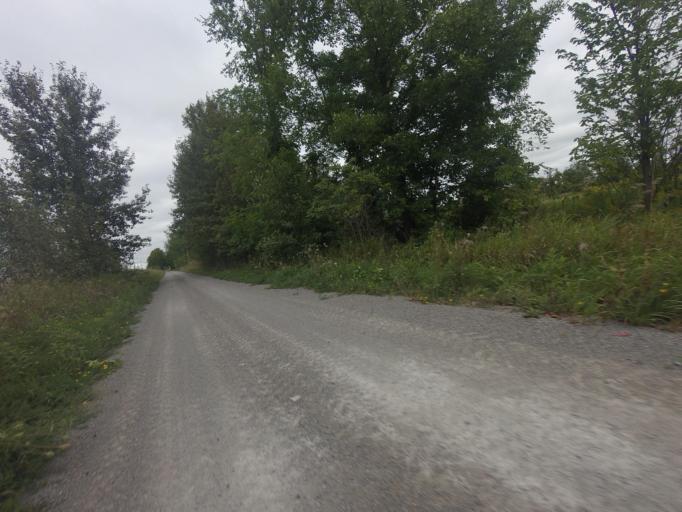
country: CA
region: Ontario
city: Omemee
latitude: 44.4546
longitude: -78.7627
